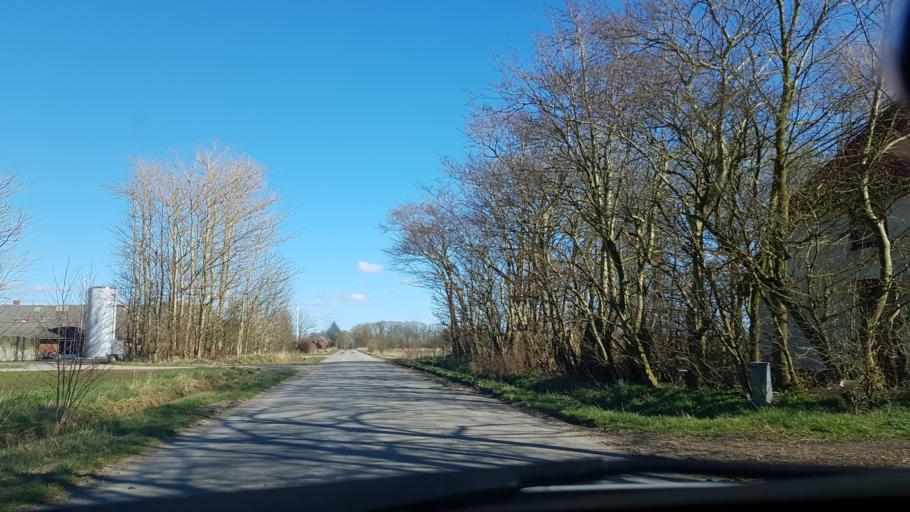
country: DK
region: South Denmark
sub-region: Tonder Kommune
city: Sherrebek
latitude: 55.2286
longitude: 8.7868
